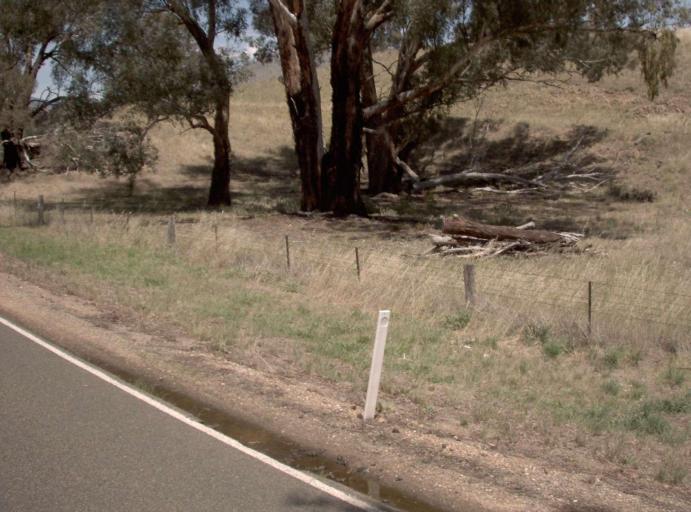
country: AU
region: Victoria
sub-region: East Gippsland
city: Bairnsdale
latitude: -37.2304
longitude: 147.7166
